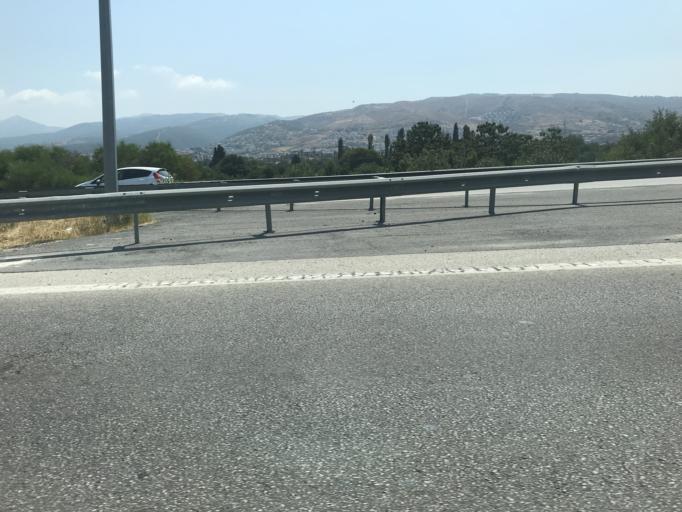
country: TR
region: Izmir
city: Urla
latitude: 38.3641
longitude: 26.8648
